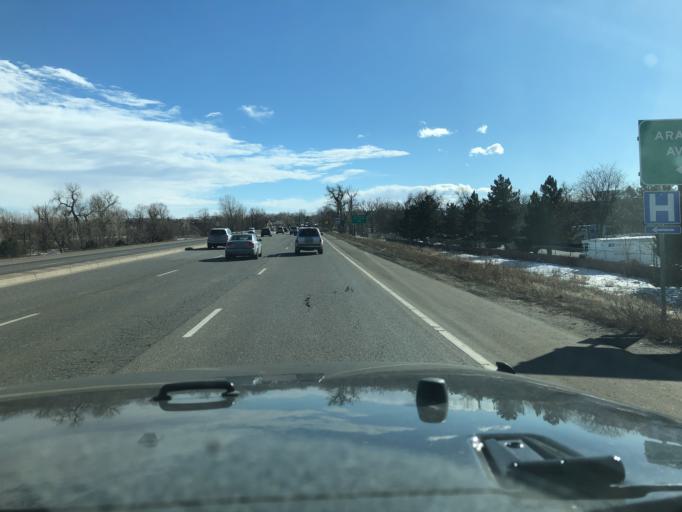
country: US
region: Colorado
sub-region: Boulder County
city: Boulder
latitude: 40.0184
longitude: -105.2435
